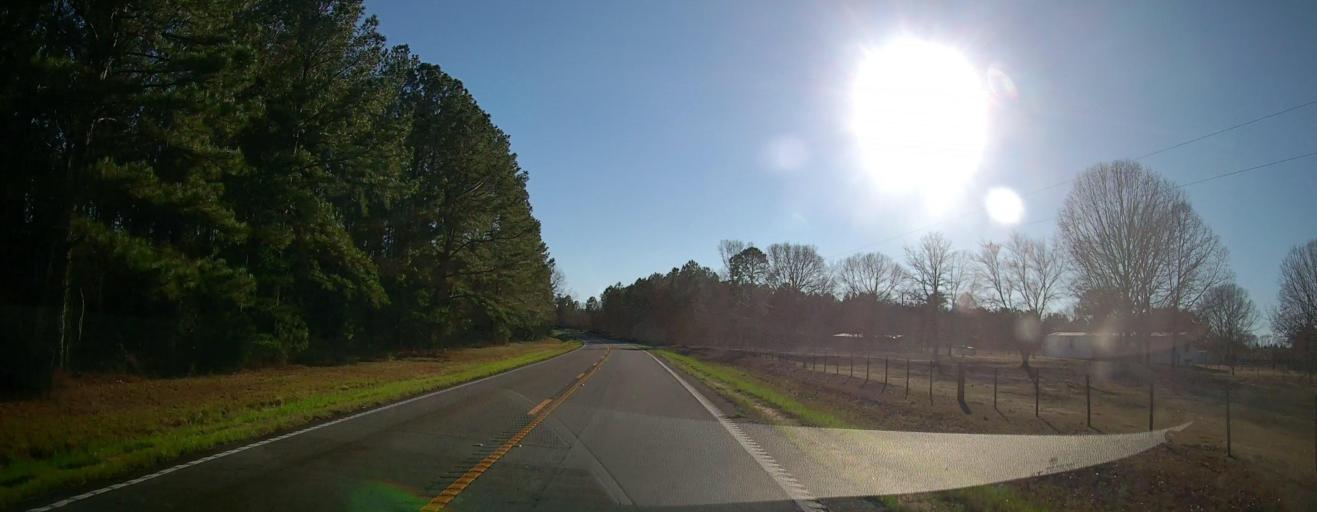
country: US
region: Georgia
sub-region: Taylor County
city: Butler
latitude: 32.5196
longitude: -84.3204
